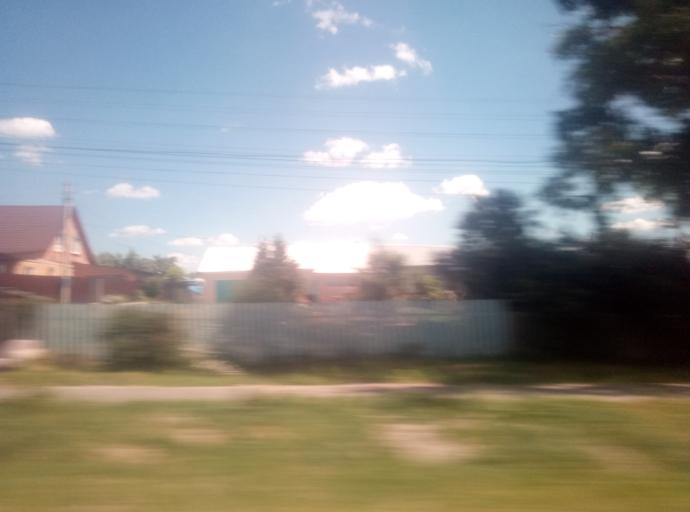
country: RU
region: Tula
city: Kireyevsk
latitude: 53.9870
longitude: 37.9318
